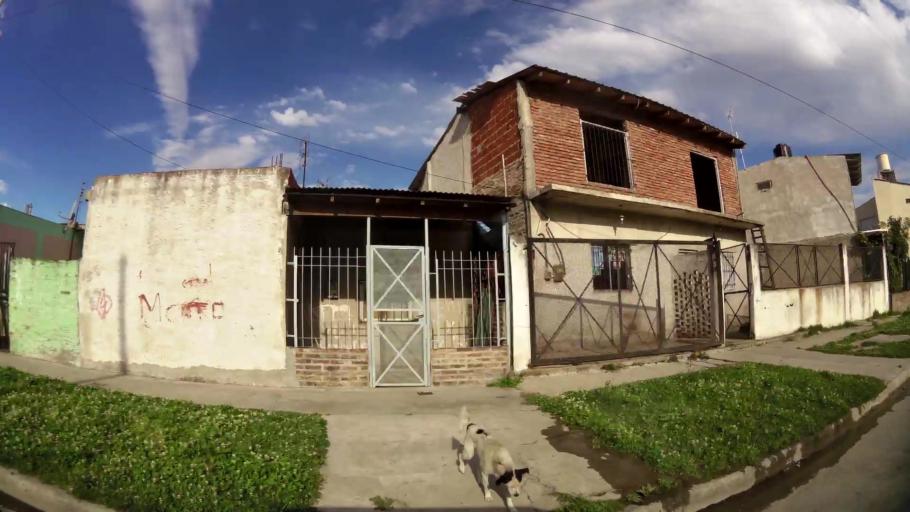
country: AR
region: Buenos Aires
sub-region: Partido de Lanus
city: Lanus
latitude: -34.7016
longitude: -58.3583
